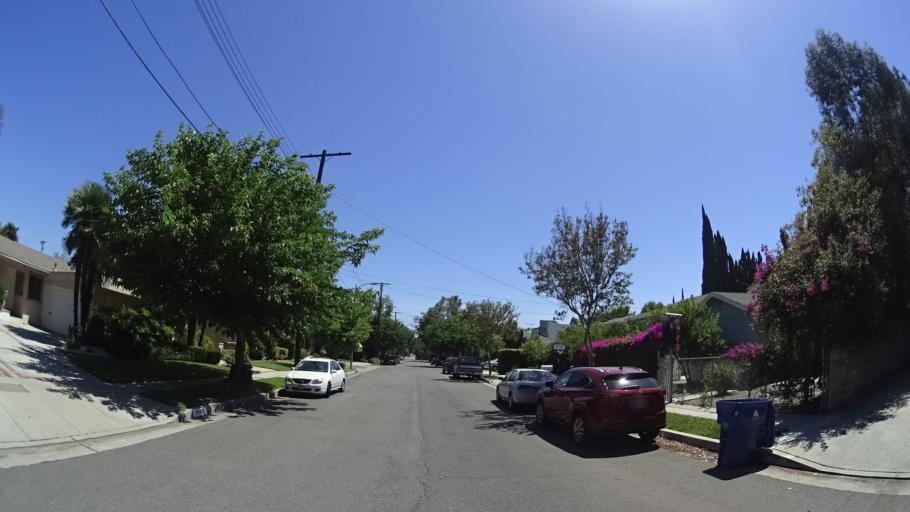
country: US
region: California
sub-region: Los Angeles County
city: North Hollywood
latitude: 34.1778
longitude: -118.4043
